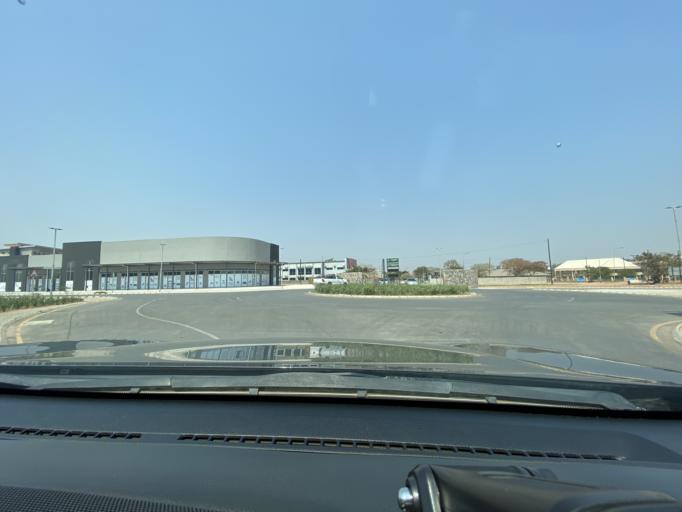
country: ZM
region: Lusaka
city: Lusaka
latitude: -15.3925
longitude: 28.3221
